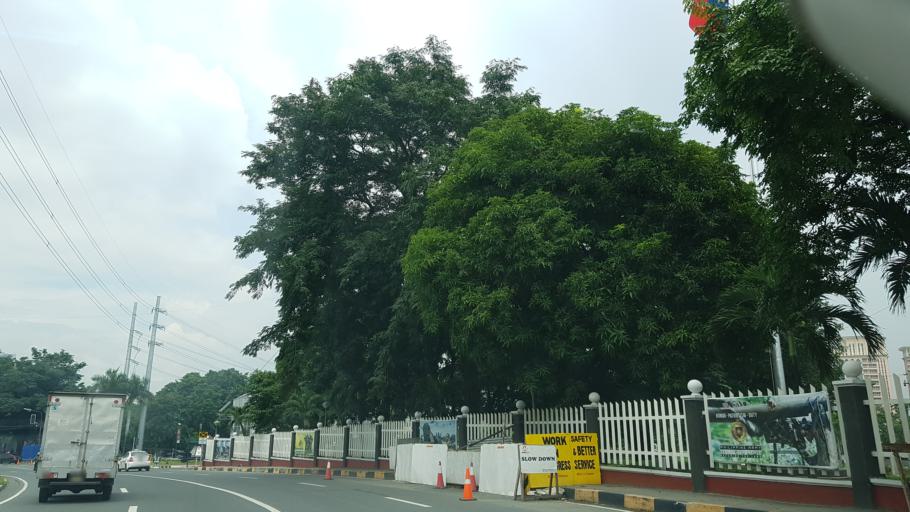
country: PH
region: Metro Manila
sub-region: Makati City
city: Makati City
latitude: 14.5347
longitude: 121.0458
